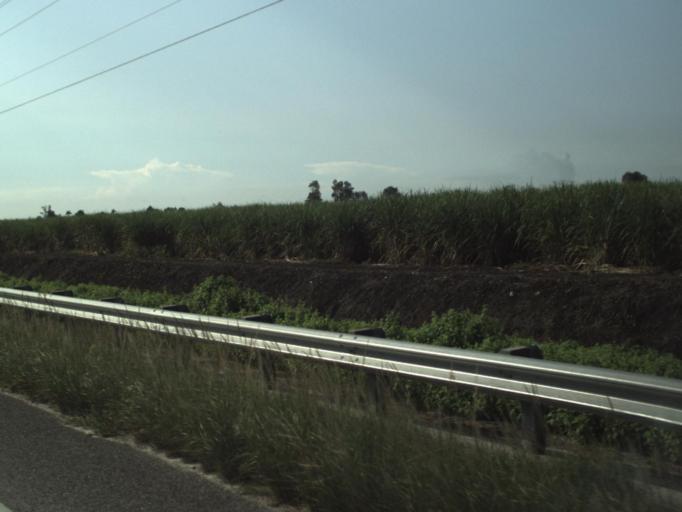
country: US
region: Florida
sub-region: Palm Beach County
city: South Bay
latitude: 26.6973
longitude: -80.7803
